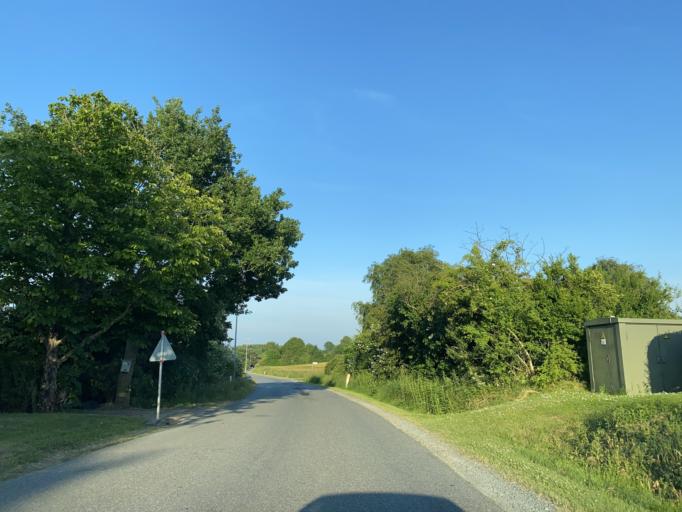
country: DK
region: South Denmark
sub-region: Aabenraa Kommune
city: Lojt Kirkeby
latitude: 55.1584
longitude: 9.4691
